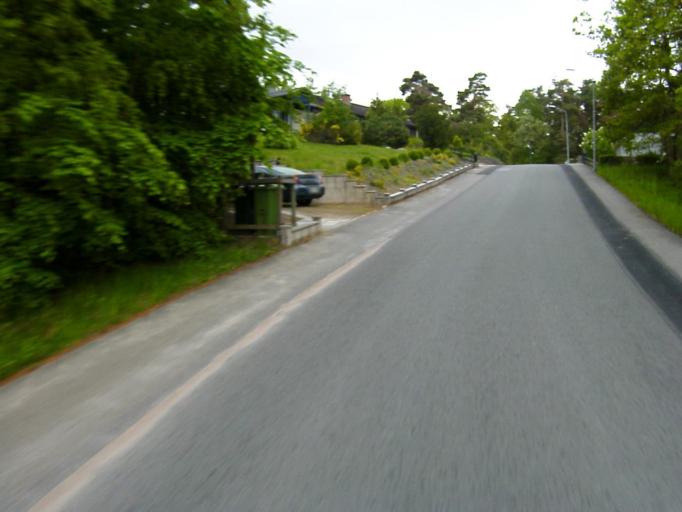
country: SE
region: Skane
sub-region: Kristianstads Kommun
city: Degeberga
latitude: 55.8342
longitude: 14.0929
